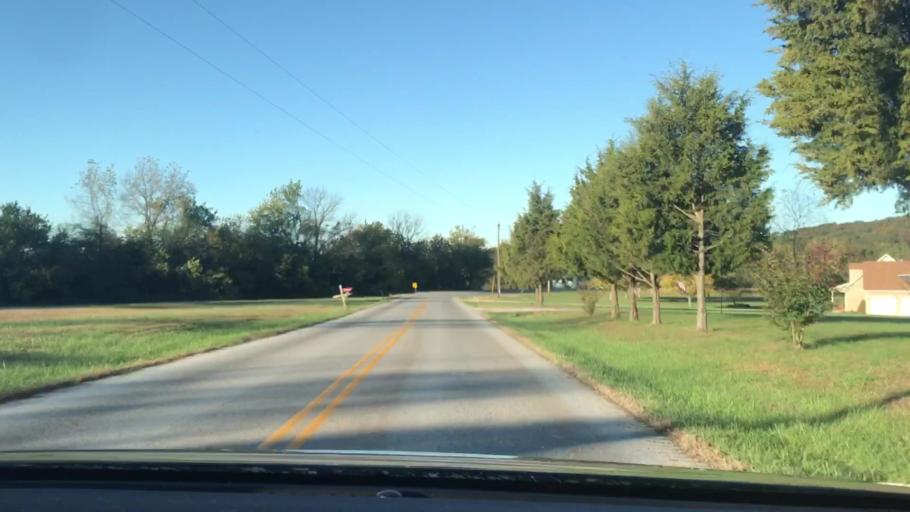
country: US
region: Kentucky
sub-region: Logan County
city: Auburn
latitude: 36.8182
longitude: -86.6556
